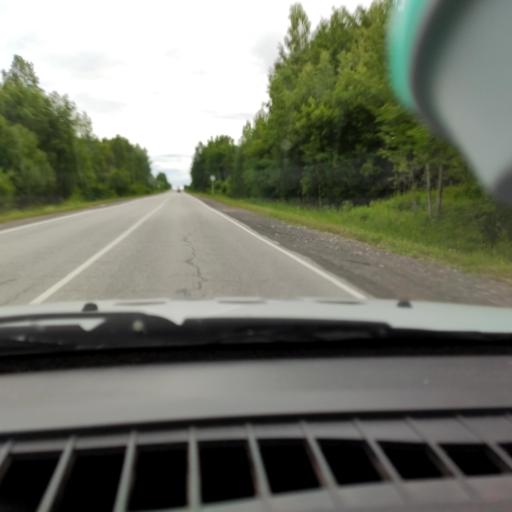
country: RU
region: Perm
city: Lys'va
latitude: 58.1417
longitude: 57.7459
